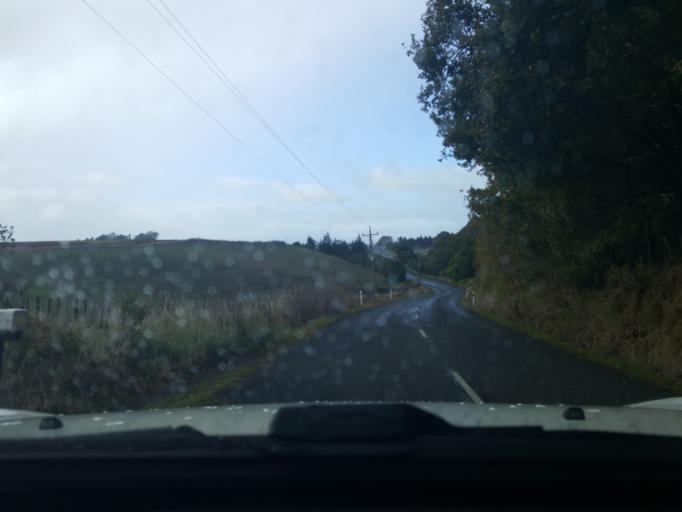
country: NZ
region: Auckland
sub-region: Auckland
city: Pukekohe East
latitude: -37.3523
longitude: 174.9932
